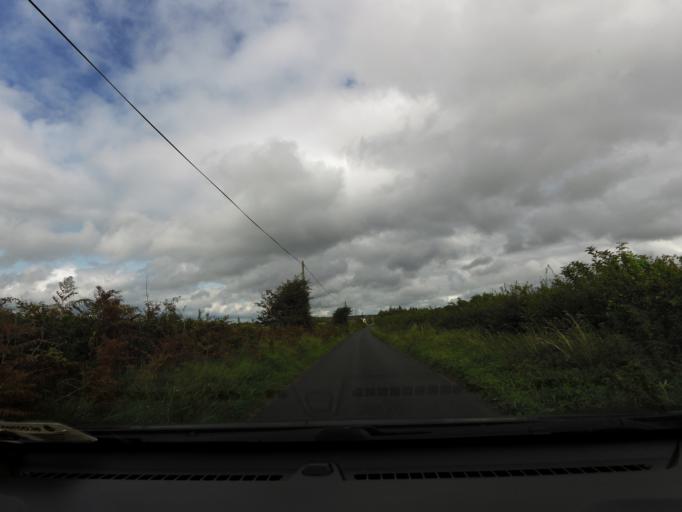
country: IE
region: Connaught
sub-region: County Galway
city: Athenry
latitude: 53.2814
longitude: -8.6686
